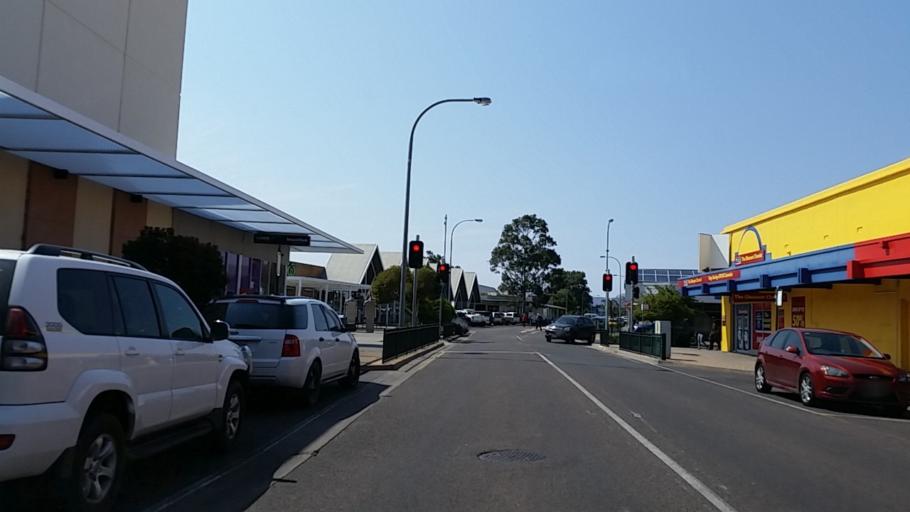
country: AU
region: South Australia
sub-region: Port Augusta
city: Port Augusta West
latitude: -32.4909
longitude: 137.7609
